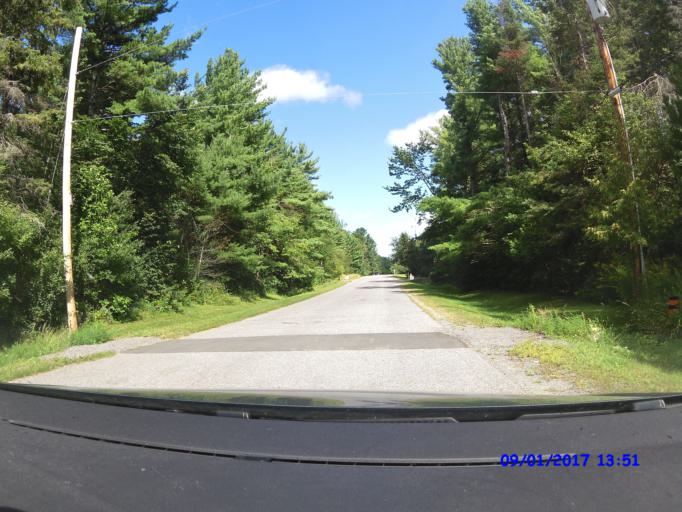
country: CA
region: Ontario
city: Bells Corners
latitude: 45.3617
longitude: -75.9647
